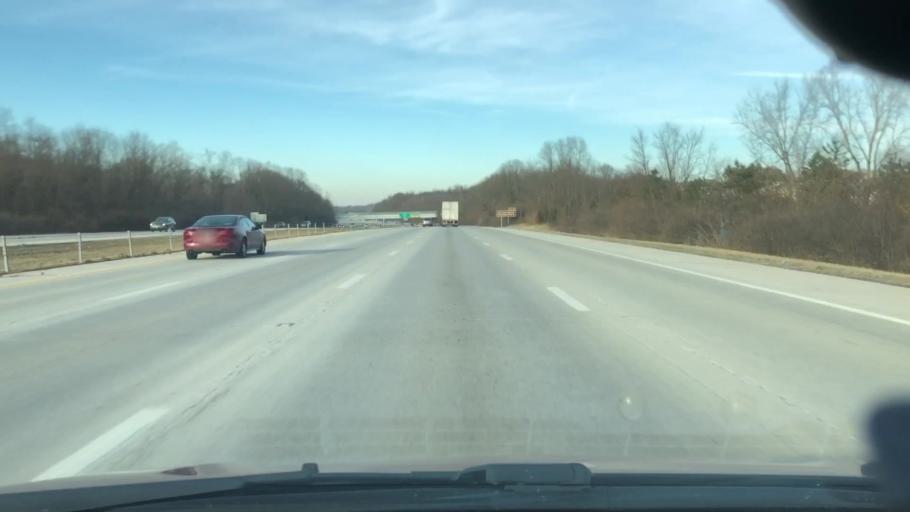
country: US
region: Ohio
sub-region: Montgomery County
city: Riverside
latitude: 39.7515
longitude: -84.0925
